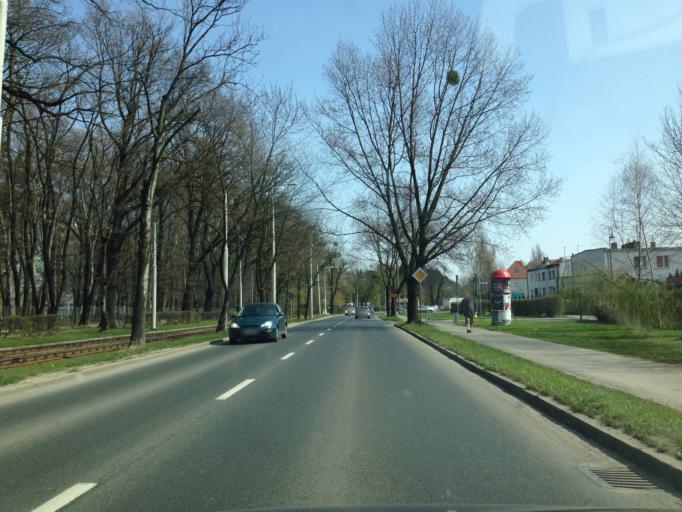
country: PL
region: Lower Silesian Voivodeship
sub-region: Powiat wroclawski
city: Wilczyce
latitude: 51.1139
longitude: 17.1000
